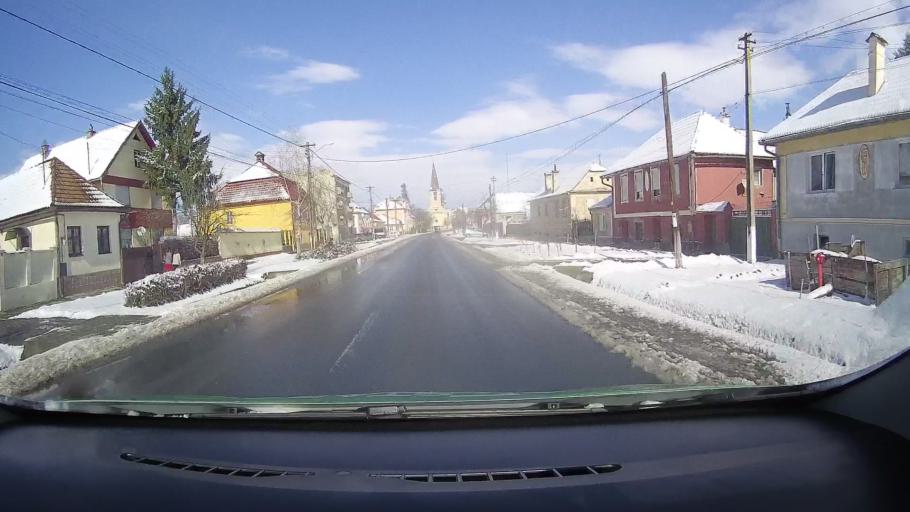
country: RO
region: Sibiu
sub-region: Comuna Nocrich
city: Nocrich
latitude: 45.8930
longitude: 24.4539
